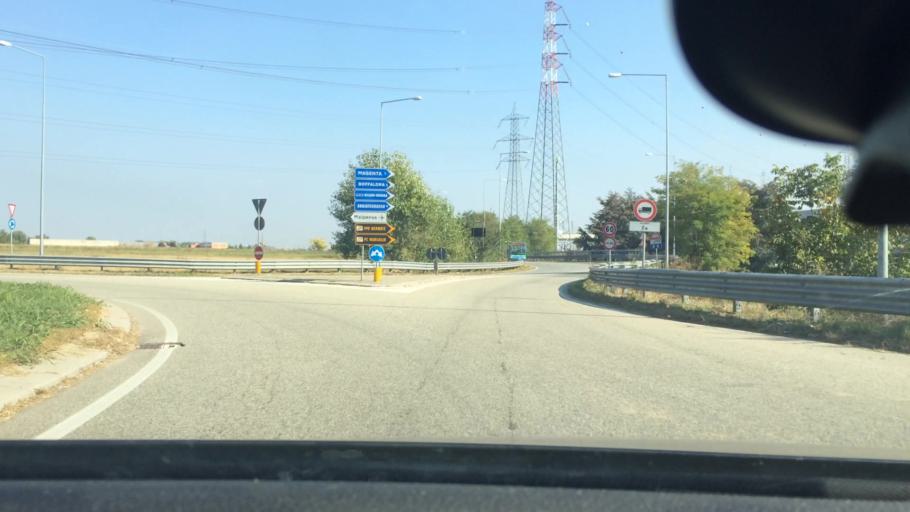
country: IT
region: Lombardy
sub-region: Citta metropolitana di Milano
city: Casate
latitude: 45.4814
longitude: 8.8321
